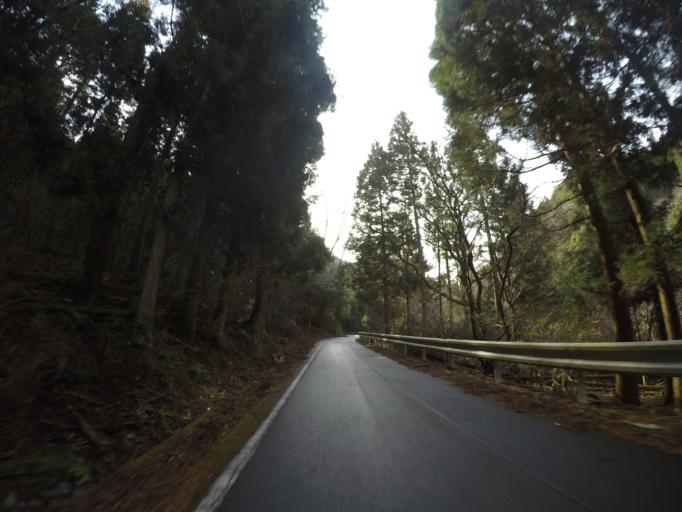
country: JP
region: Shizuoka
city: Heda
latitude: 34.8854
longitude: 138.8638
